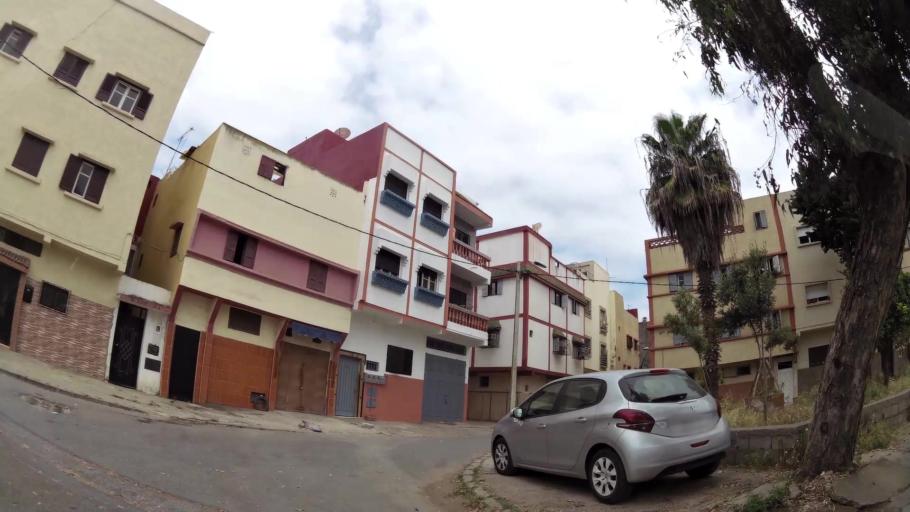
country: MA
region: Rabat-Sale-Zemmour-Zaer
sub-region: Rabat
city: Rabat
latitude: 34.0004
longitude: -6.8626
